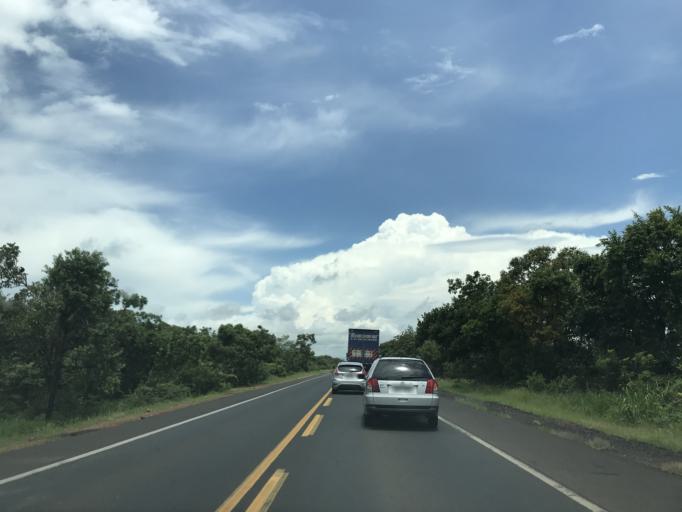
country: BR
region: Minas Gerais
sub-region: Frutal
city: Frutal
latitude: -19.6842
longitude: -48.9859
